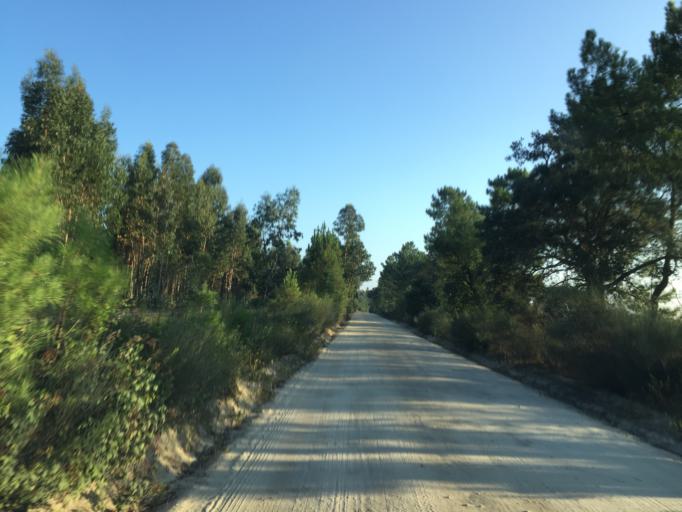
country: PT
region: Portalegre
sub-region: Ponte de Sor
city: Santo Andre
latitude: 39.1522
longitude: -8.3025
